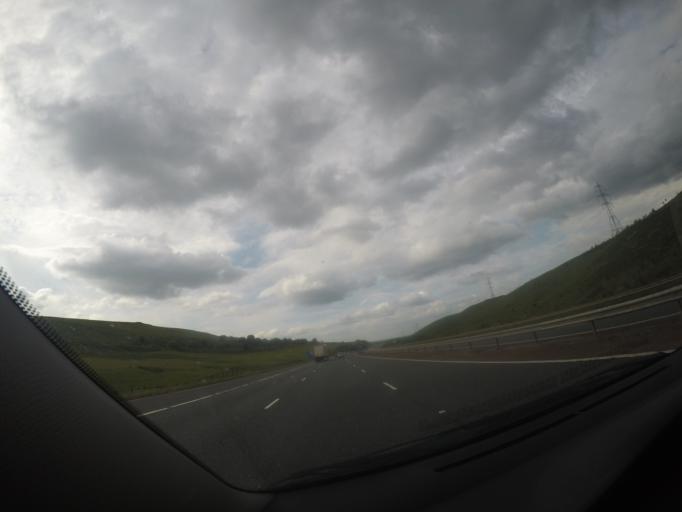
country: GB
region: Scotland
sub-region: South Lanarkshire
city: Douglas
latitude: 55.5489
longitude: -3.7998
